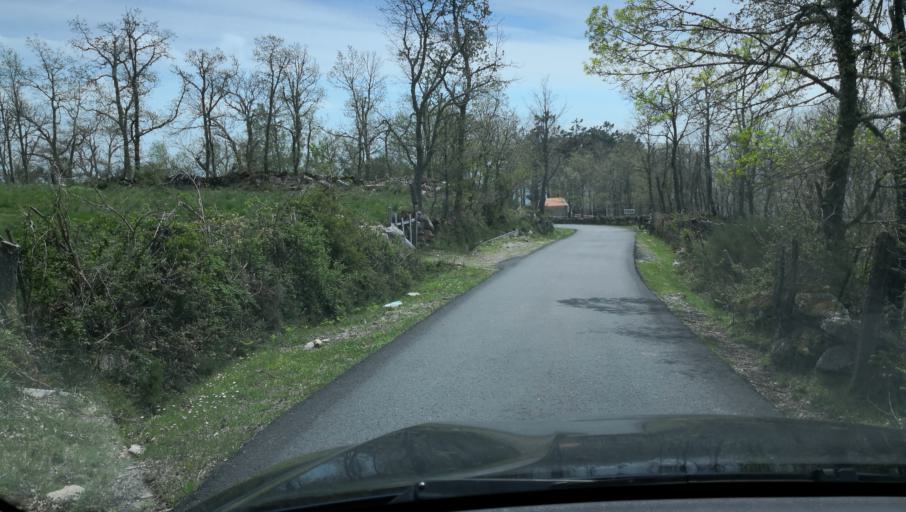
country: PT
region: Vila Real
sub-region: Vila Real
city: Vila Real
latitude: 41.2929
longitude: -7.8200
